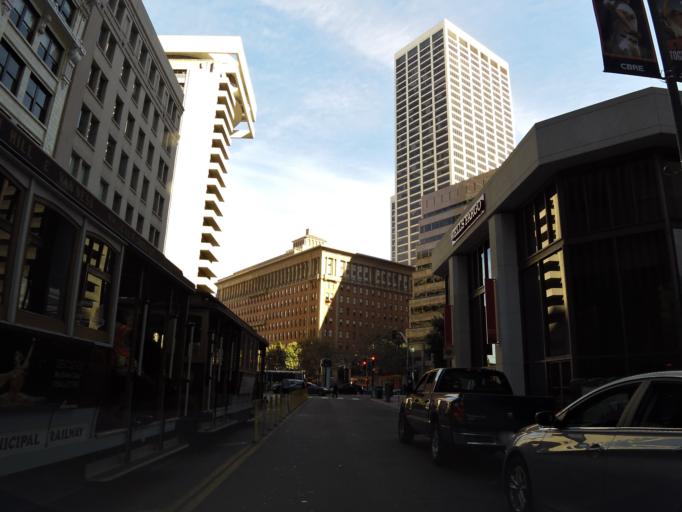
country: US
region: California
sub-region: San Francisco County
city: San Francisco
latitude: 37.7935
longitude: -122.3972
